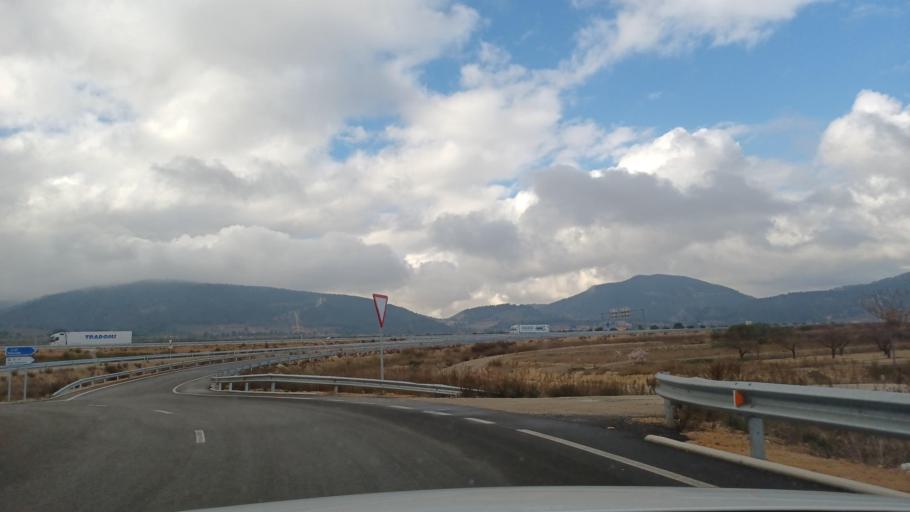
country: ES
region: Valencia
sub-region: Provincia de Valencia
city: La Font de la Figuera
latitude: 38.8171
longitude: -0.8872
